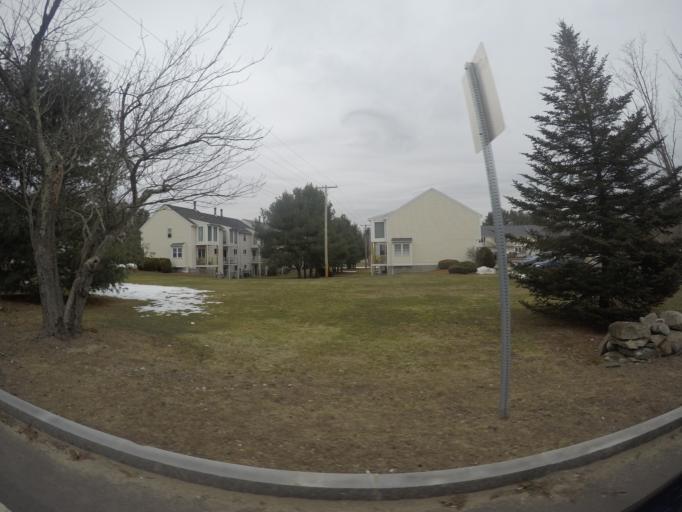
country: US
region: Massachusetts
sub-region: Plymouth County
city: West Bridgewater
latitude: 42.0105
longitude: -71.0681
